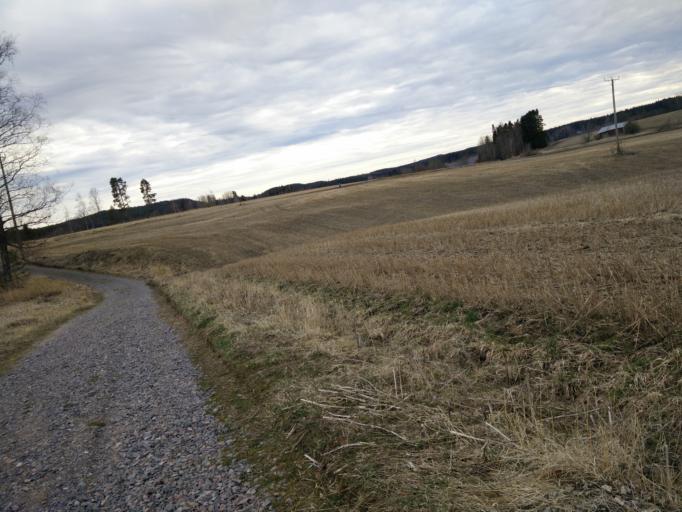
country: FI
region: Pirkanmaa
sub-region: Tampere
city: Orivesi
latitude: 61.7104
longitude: 24.3208
